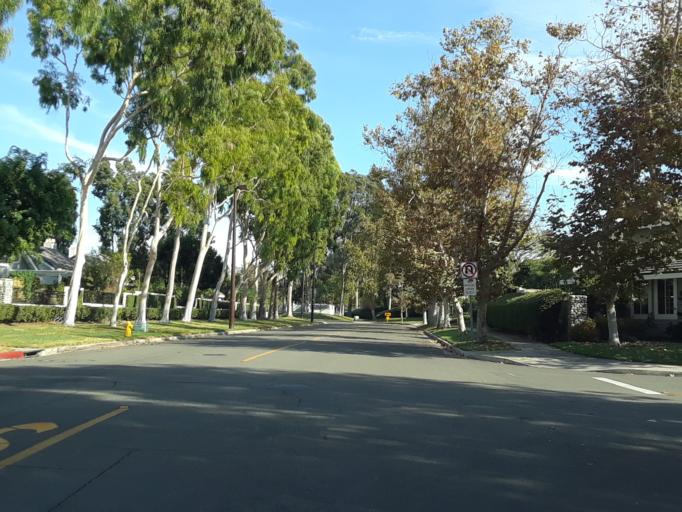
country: US
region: California
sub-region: Orange County
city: Irvine
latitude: 33.6720
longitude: -117.8079
